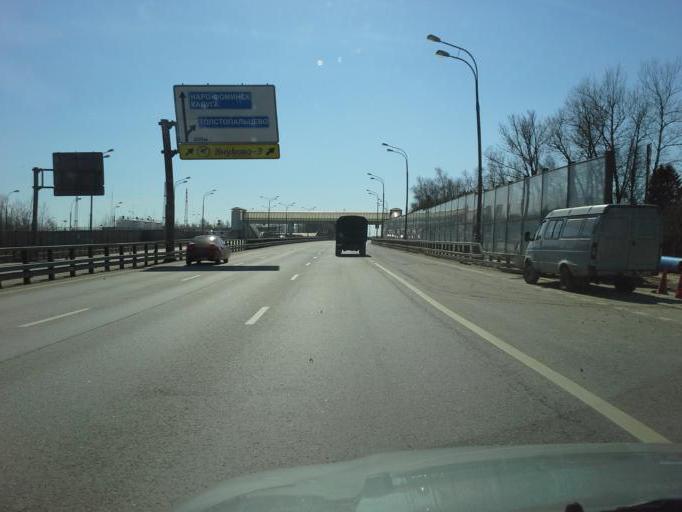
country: RU
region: Moskovskaya
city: Annino
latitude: 55.5990
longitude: 37.2432
